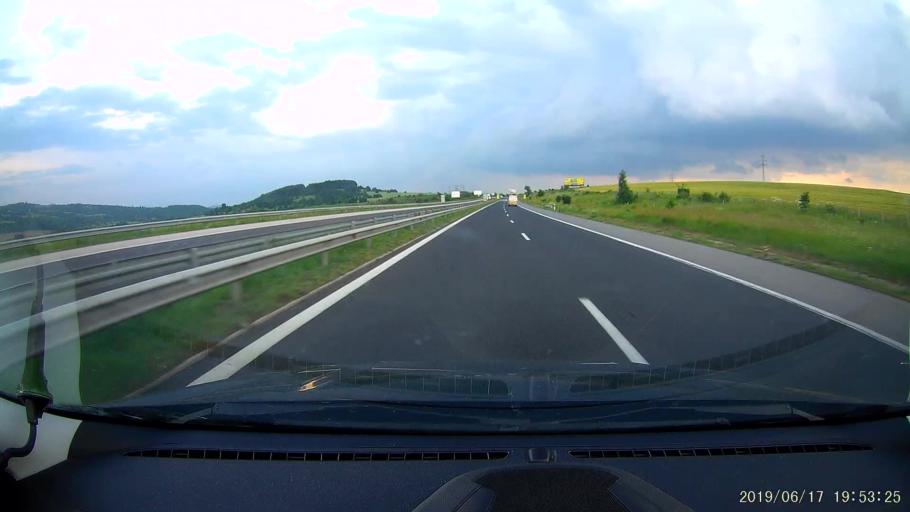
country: BG
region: Sofiya
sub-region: Obshtina Ikhtiman
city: Ikhtiman
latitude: 42.5395
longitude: 23.7223
